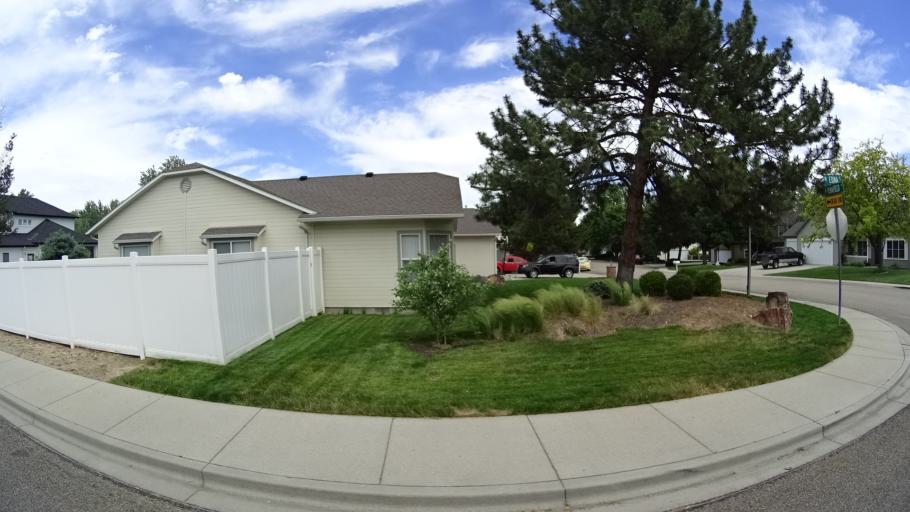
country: US
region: Idaho
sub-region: Ada County
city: Eagle
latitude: 43.6412
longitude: -116.3226
